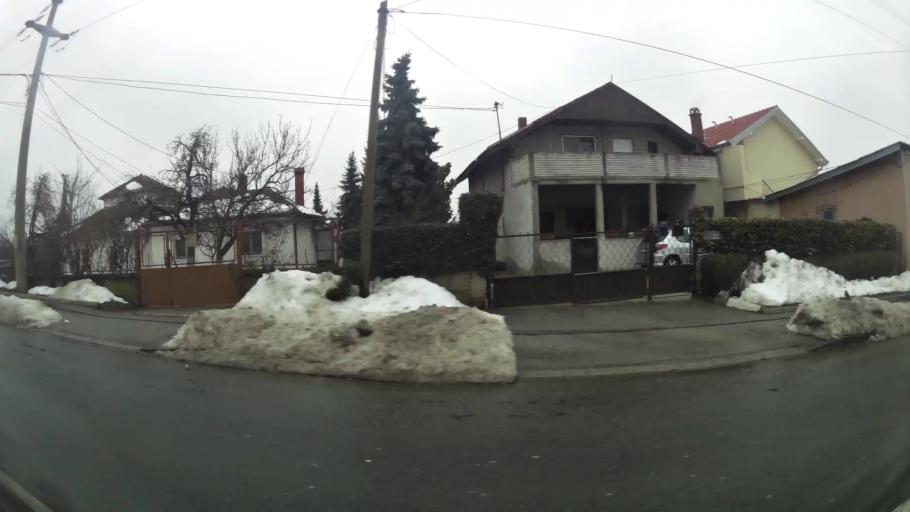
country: RS
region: Central Serbia
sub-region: Belgrade
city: Vozdovac
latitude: 44.7497
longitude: 20.4944
